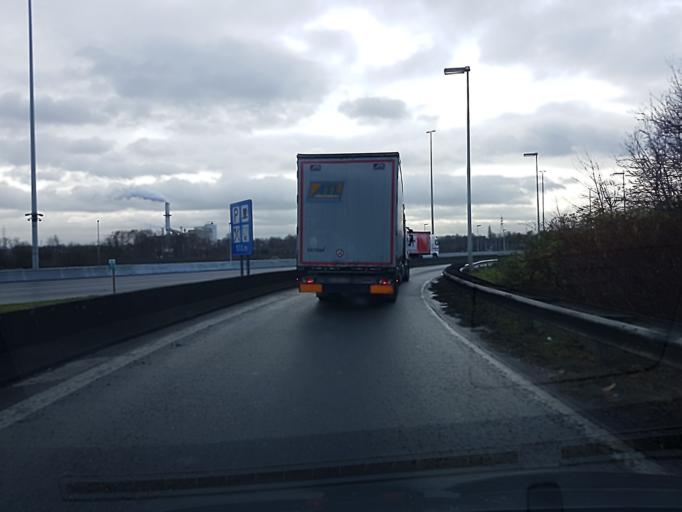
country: BE
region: Wallonia
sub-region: Province de Liege
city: Vise
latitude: 50.7527
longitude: 5.6945
